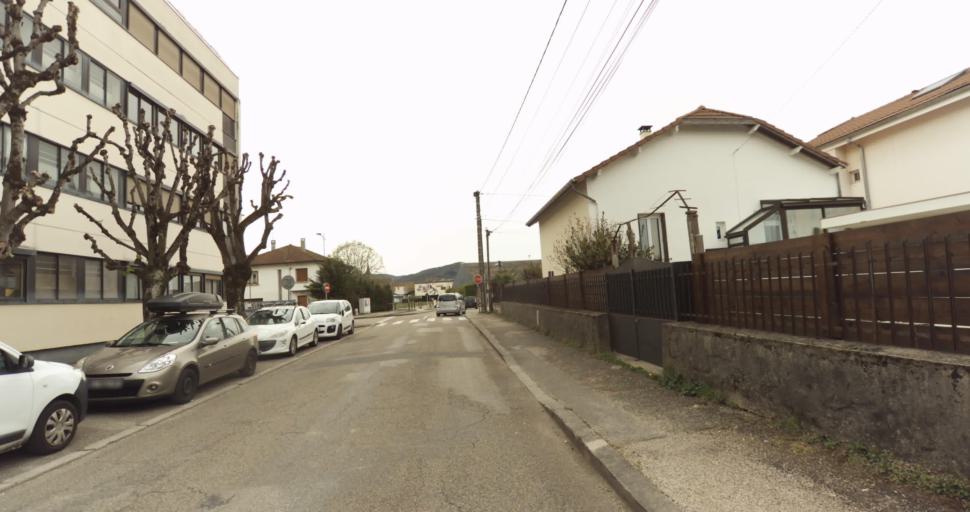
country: FR
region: Rhone-Alpes
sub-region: Departement de l'Ain
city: Amberieu-en-Bugey
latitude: 45.9619
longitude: 5.3553
